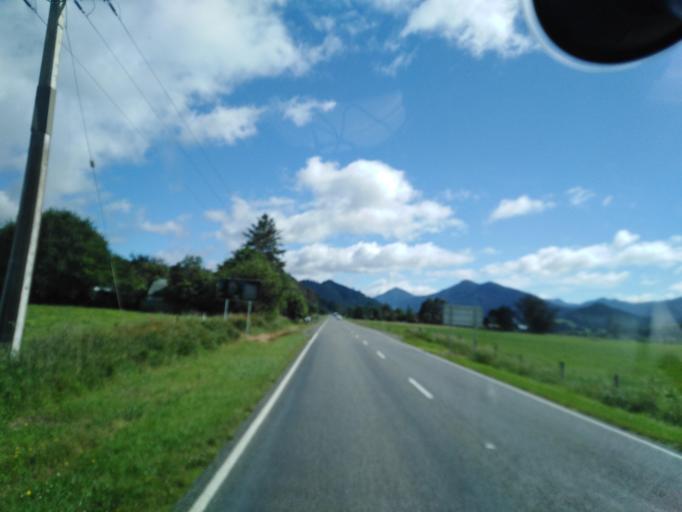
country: NZ
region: Nelson
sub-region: Nelson City
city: Nelson
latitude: -41.2412
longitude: 173.5787
